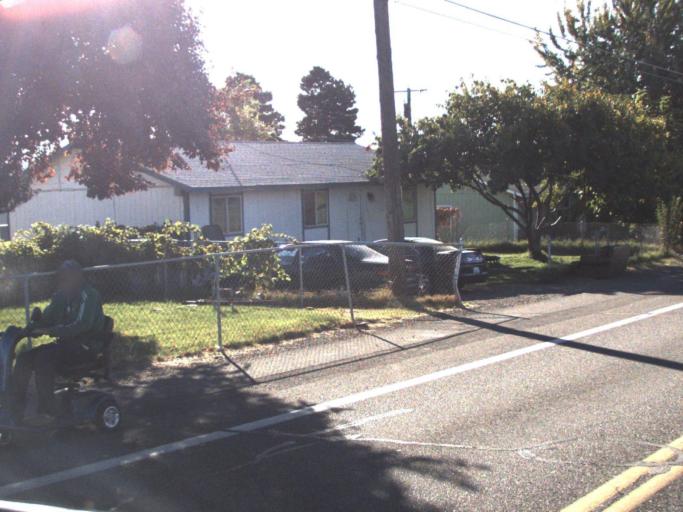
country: US
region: Washington
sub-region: Benton County
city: Benton City
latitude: 46.2768
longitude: -119.4942
